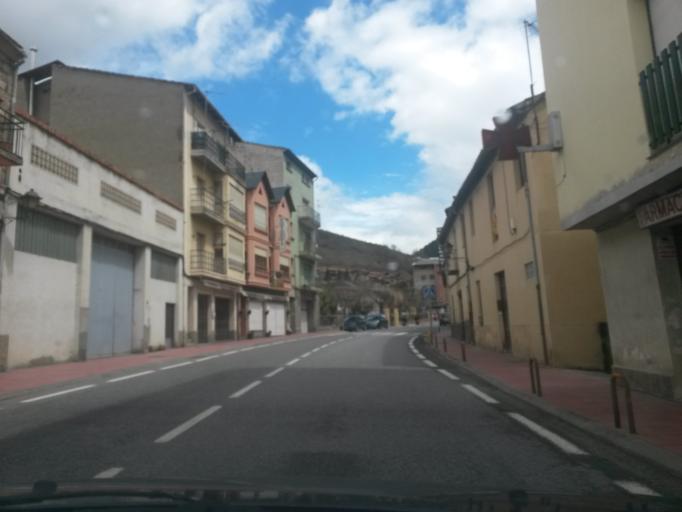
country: ES
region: Catalonia
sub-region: Provincia de Lleida
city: Lles de Cerdanya
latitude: 42.3596
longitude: 1.6941
